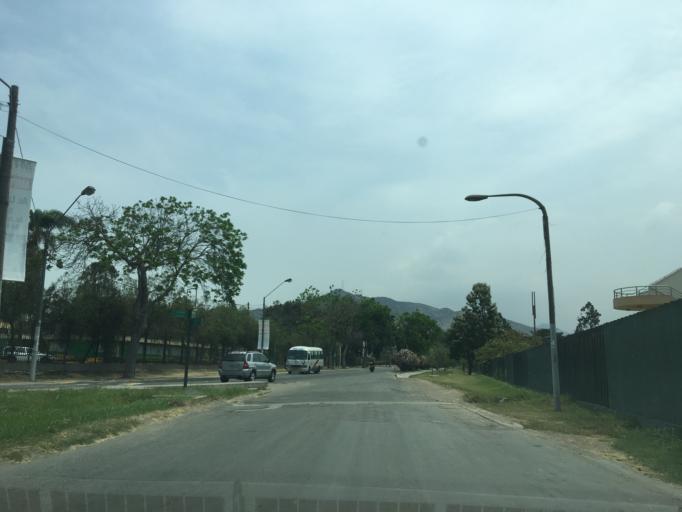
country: PE
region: Lima
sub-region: Lima
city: La Molina
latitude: -12.0797
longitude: -76.9506
